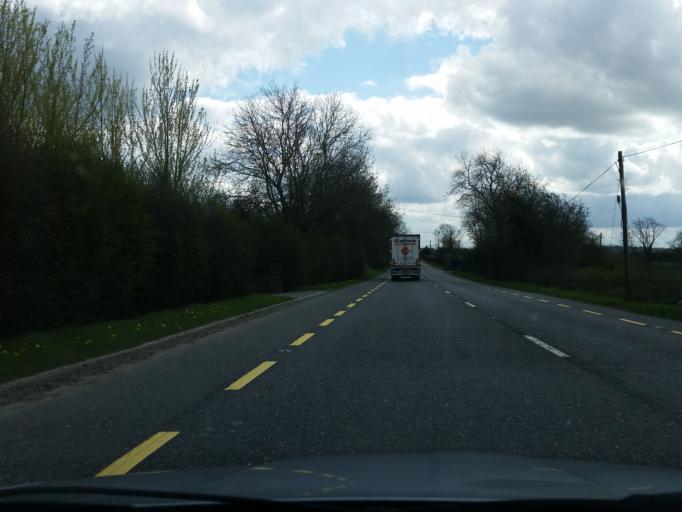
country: IE
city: Kentstown
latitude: 53.5918
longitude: -6.4640
